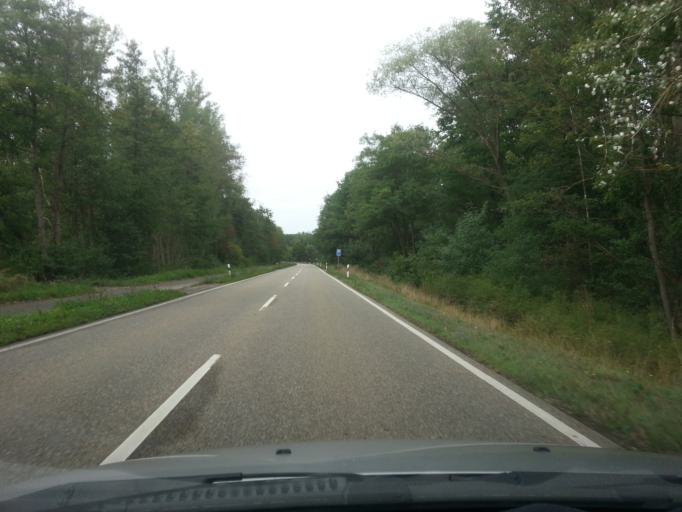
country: DE
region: Rheinland-Pfalz
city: Offenbach an der Queich
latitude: 49.2079
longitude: 8.1897
